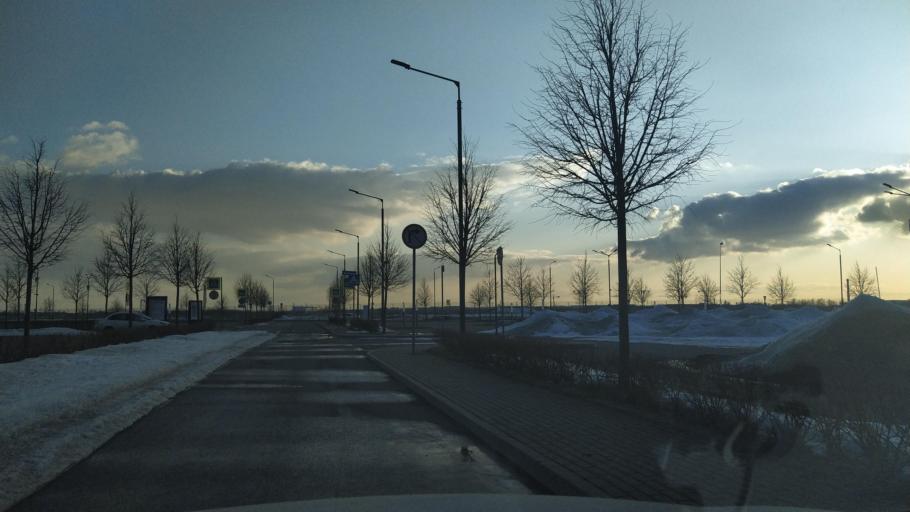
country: RU
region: St.-Petersburg
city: Aleksandrovskaya
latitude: 59.7610
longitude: 30.3510
